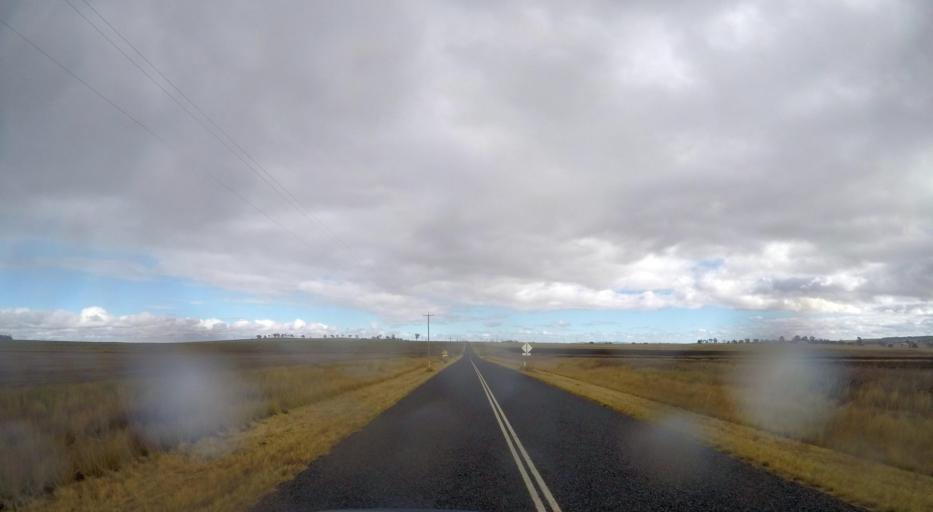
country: AU
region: Queensland
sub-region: Southern Downs
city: Warwick
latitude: -28.0545
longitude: 152.0253
